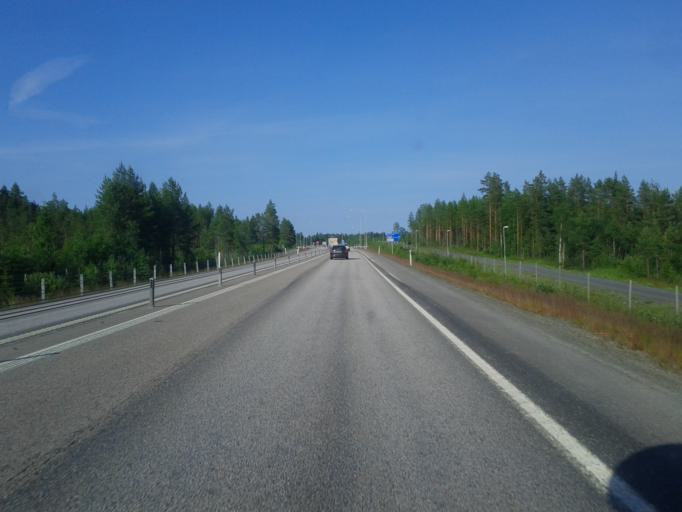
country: SE
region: Vaesterbotten
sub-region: Umea Kommun
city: Saevar
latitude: 63.8896
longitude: 20.5166
